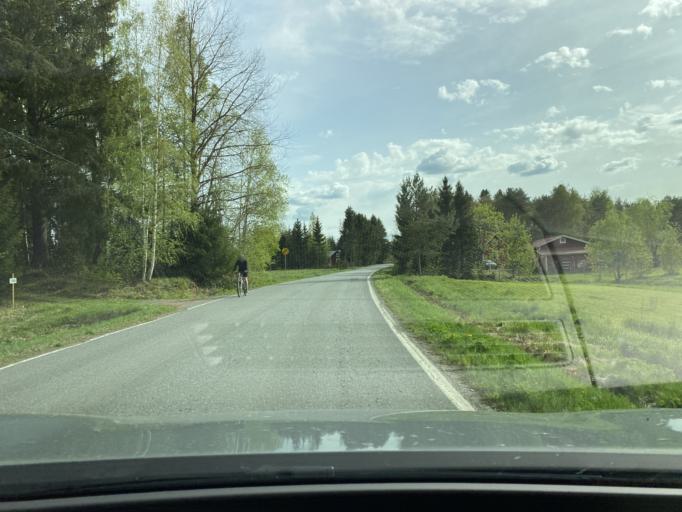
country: FI
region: Varsinais-Suomi
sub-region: Salo
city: Kiikala
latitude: 60.5221
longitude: 23.5424
